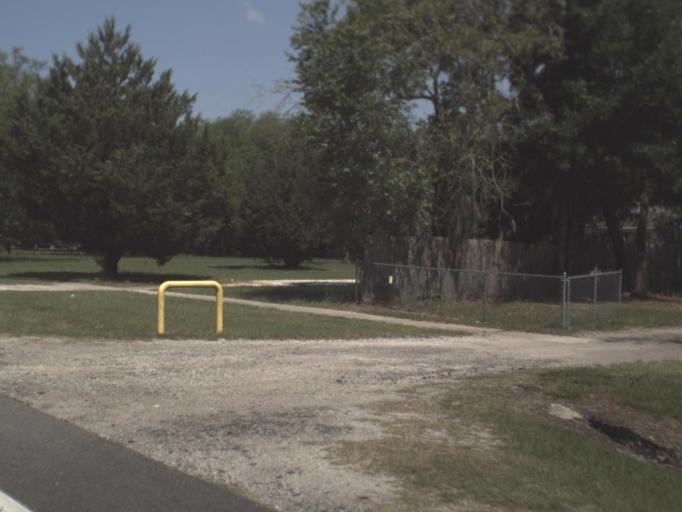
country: US
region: Florida
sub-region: Clay County
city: Green Cove Springs
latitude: 29.9838
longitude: -81.7232
